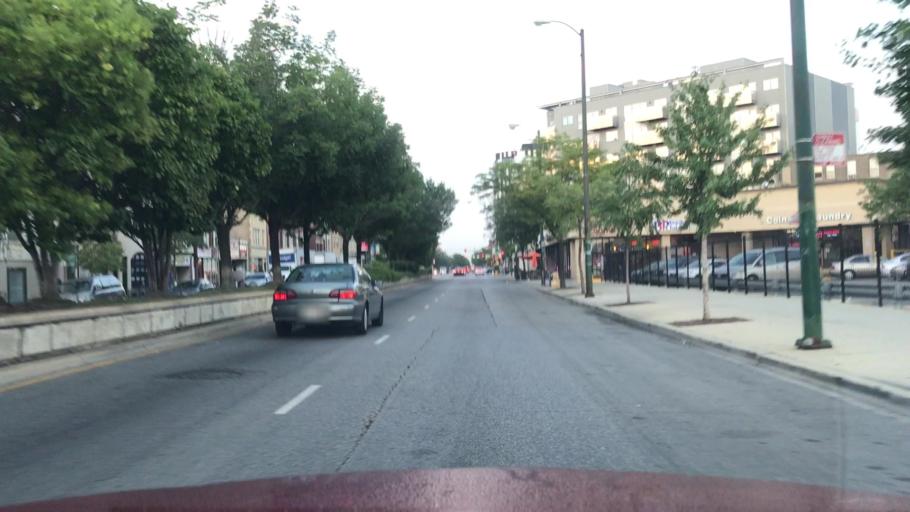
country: US
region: Illinois
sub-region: Cook County
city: Chicago
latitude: 41.9058
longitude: -87.6676
